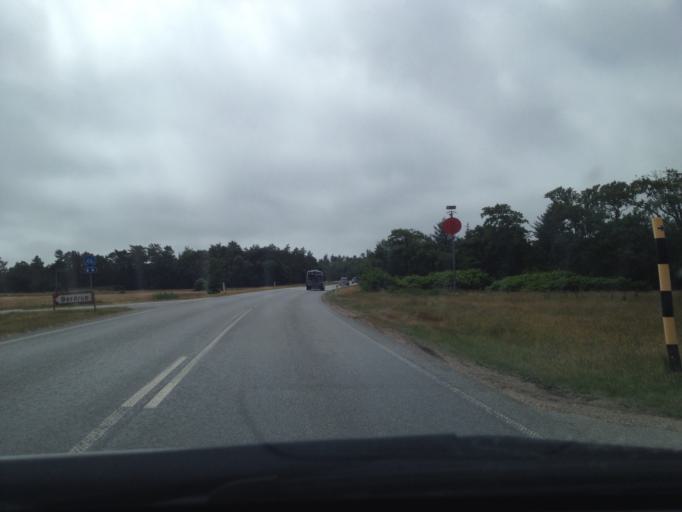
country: DK
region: South Denmark
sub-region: Varde Kommune
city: Oksbol
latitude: 55.5931
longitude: 8.2268
